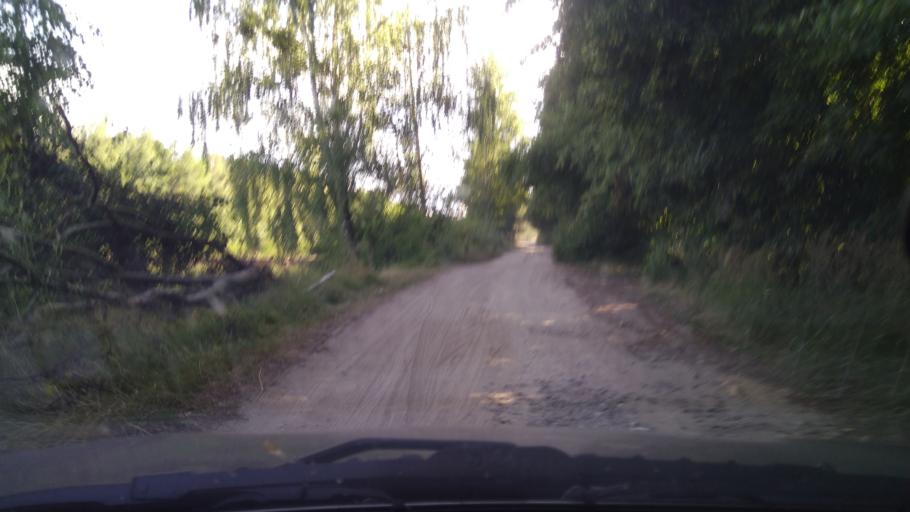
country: BY
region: Brest
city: Byelaazyorsk
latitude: 52.4465
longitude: 25.1780
